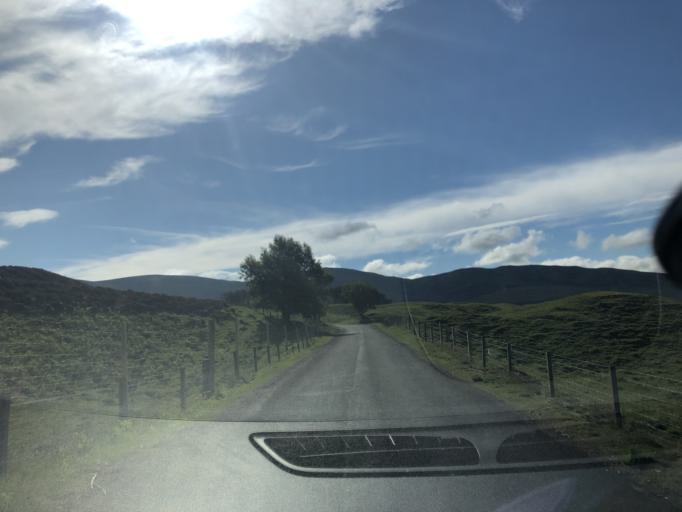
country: GB
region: Scotland
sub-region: Angus
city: Kirriemuir
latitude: 56.8280
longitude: -3.0559
